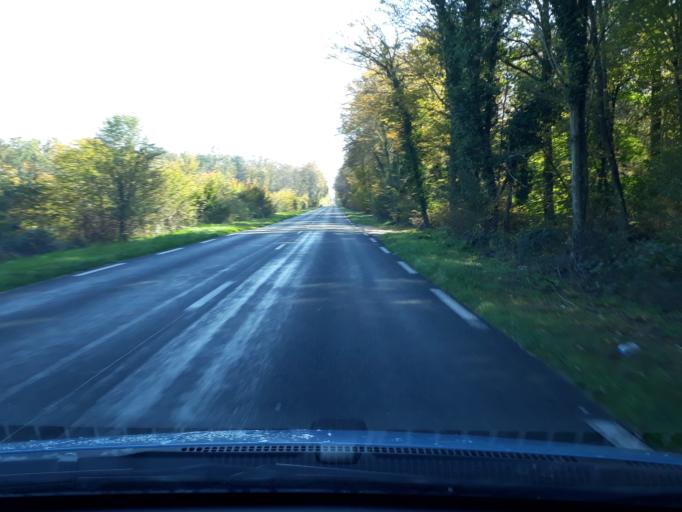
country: FR
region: Ile-de-France
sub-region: Departement de Seine-et-Marne
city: Bois-le-Roi
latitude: 48.4542
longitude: 2.7053
